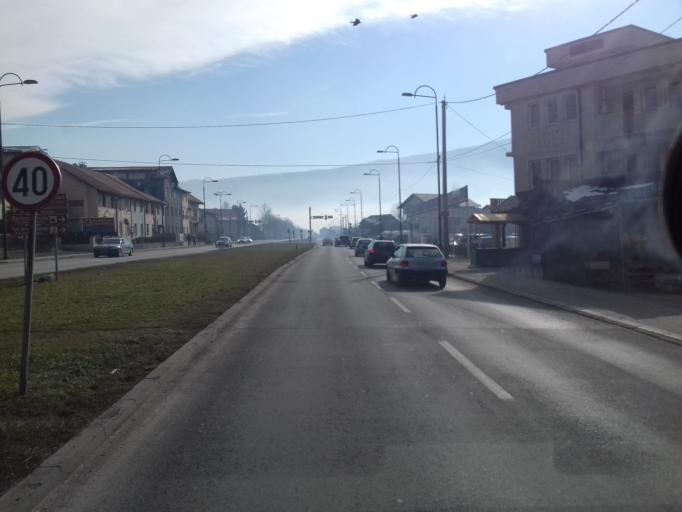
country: BA
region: Federation of Bosnia and Herzegovina
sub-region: Kanton Sarajevo
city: Sarajevo
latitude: 43.8171
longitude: 18.3082
